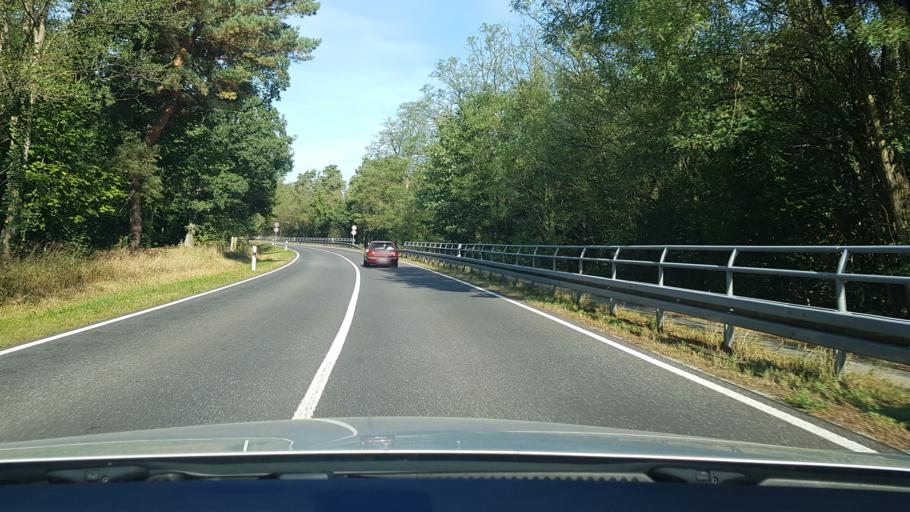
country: DE
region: Brandenburg
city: Mixdorf
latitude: 52.1465
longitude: 14.4152
